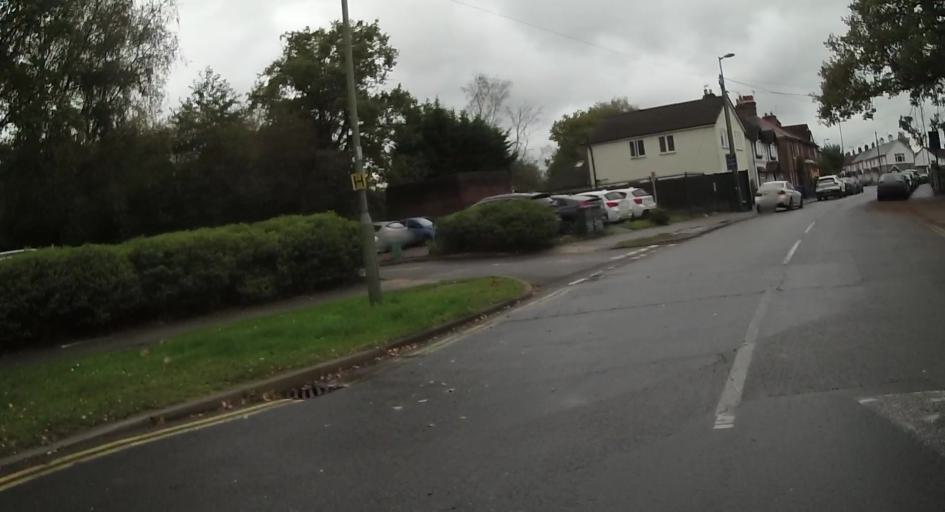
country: GB
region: England
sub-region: Surrey
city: Woking
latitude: 51.3266
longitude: -0.5383
